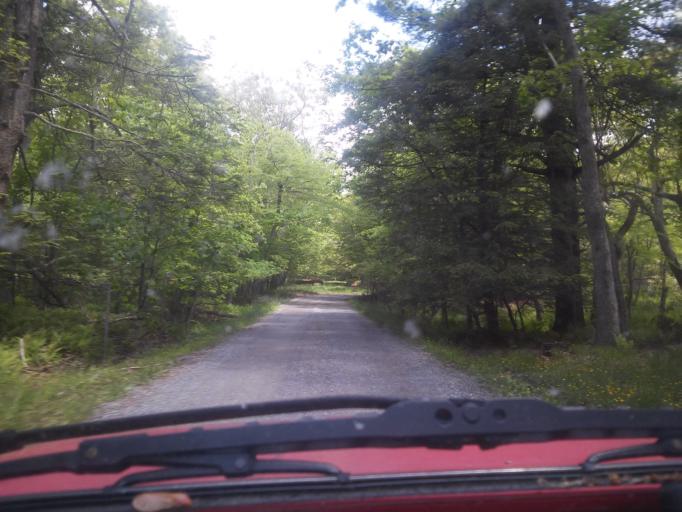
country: US
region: Virginia
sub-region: Giles County
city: Pembroke
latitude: 37.3743
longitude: -80.5236
